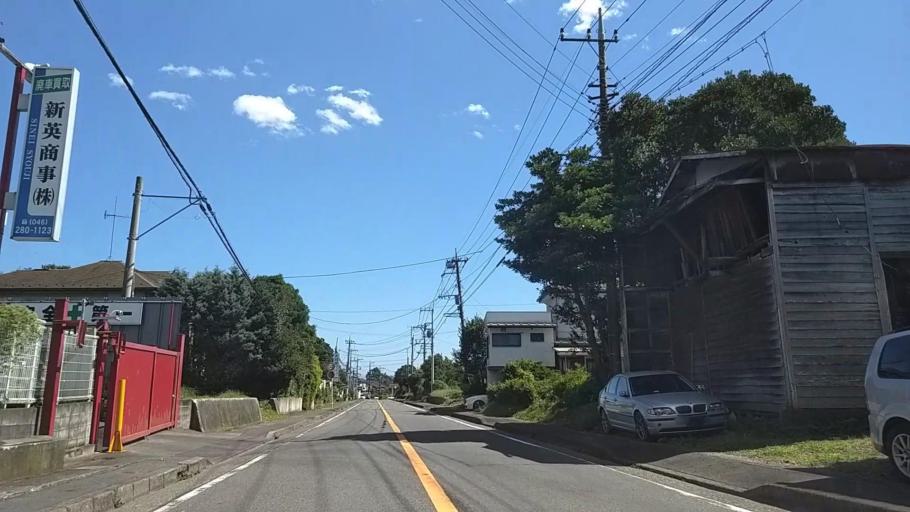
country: JP
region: Kanagawa
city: Zama
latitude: 35.5419
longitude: 139.3013
